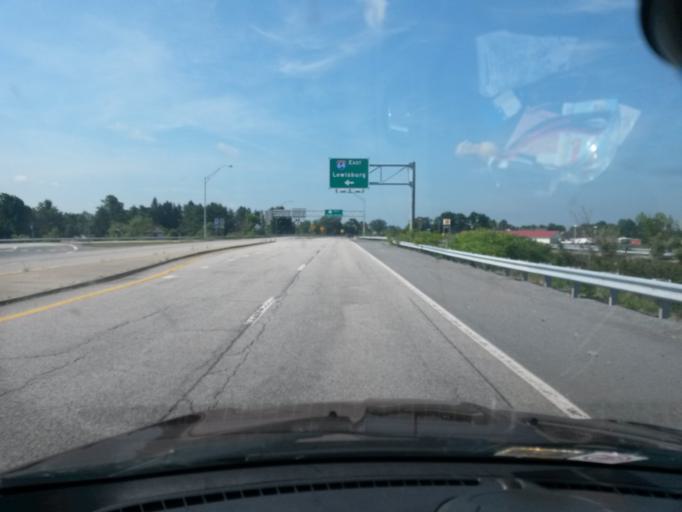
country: US
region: West Virginia
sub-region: Raleigh County
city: Daniels
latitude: 37.7728
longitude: -81.0664
